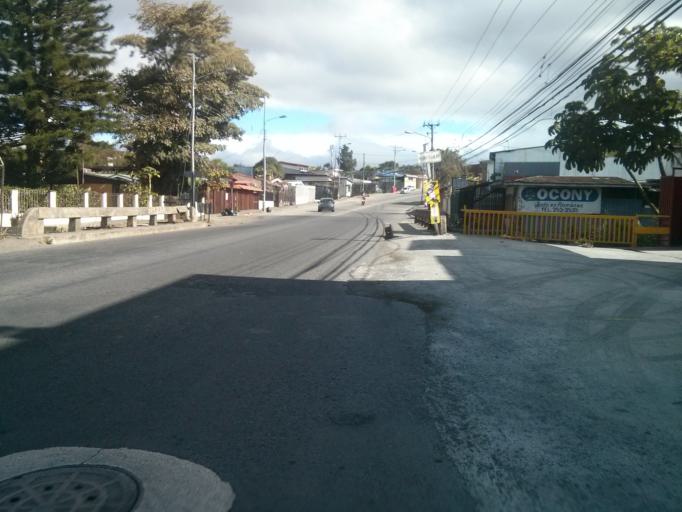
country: CR
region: San Jose
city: San Pedro
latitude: 9.9136
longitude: -84.0566
